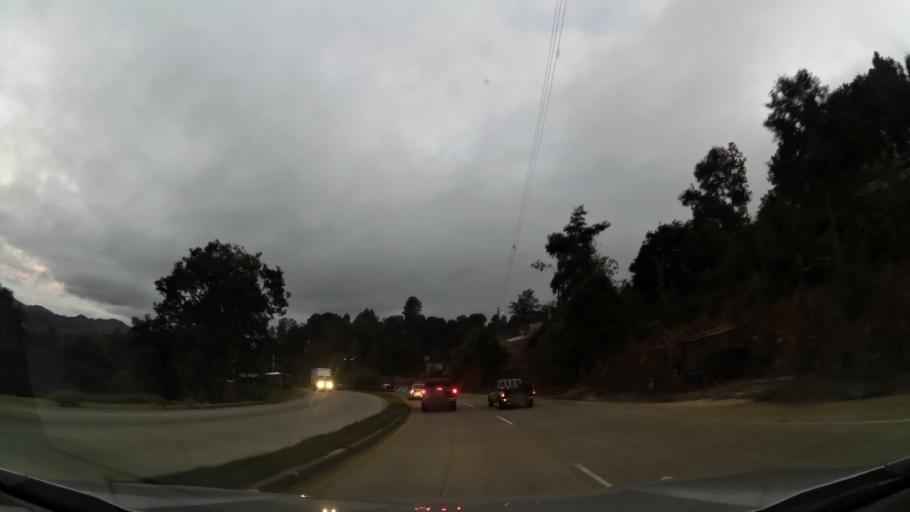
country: GT
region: Chimaltenango
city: Santa Apolonia
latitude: 14.8507
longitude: -91.0507
